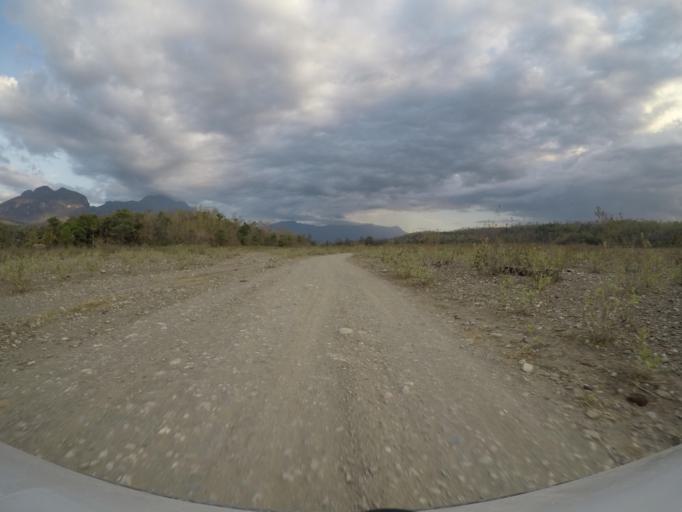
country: TL
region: Bobonaro
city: Maliana
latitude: -8.8955
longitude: 125.2084
